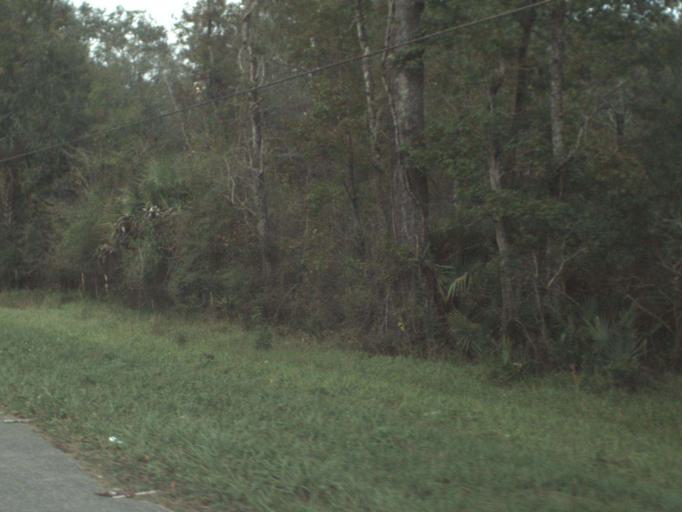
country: US
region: Florida
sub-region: Leon County
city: Woodville
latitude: 30.2301
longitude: -84.2291
